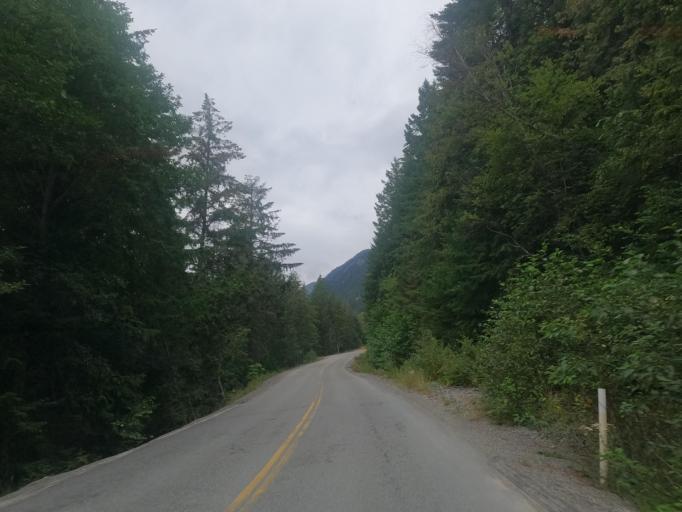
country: CA
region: British Columbia
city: Pemberton
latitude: 50.3010
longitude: -122.5839
